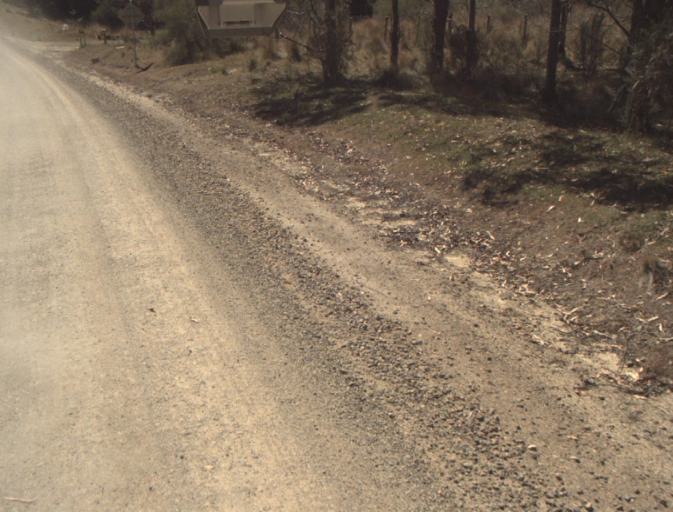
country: AU
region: Tasmania
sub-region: Dorset
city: Scottsdale
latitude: -41.3618
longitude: 147.4620
